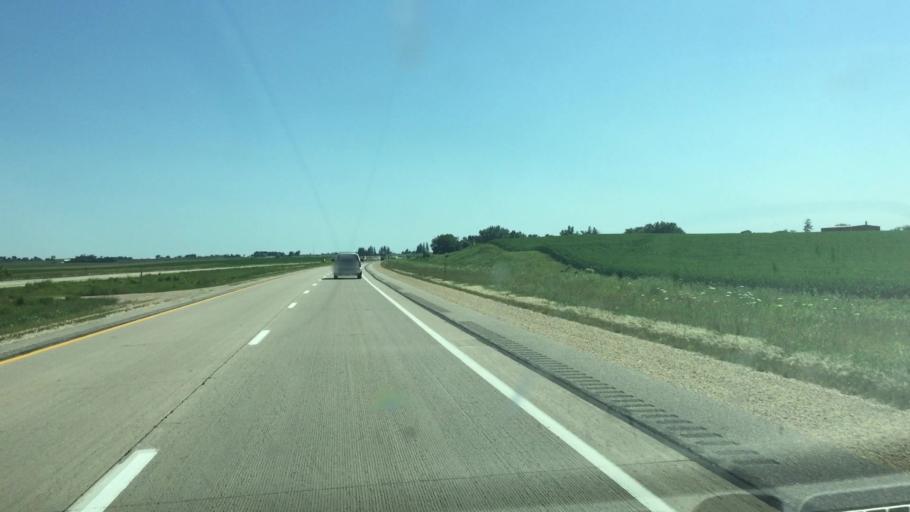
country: US
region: Iowa
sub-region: Jones County
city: Monticello
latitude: 42.1907
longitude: -91.2172
